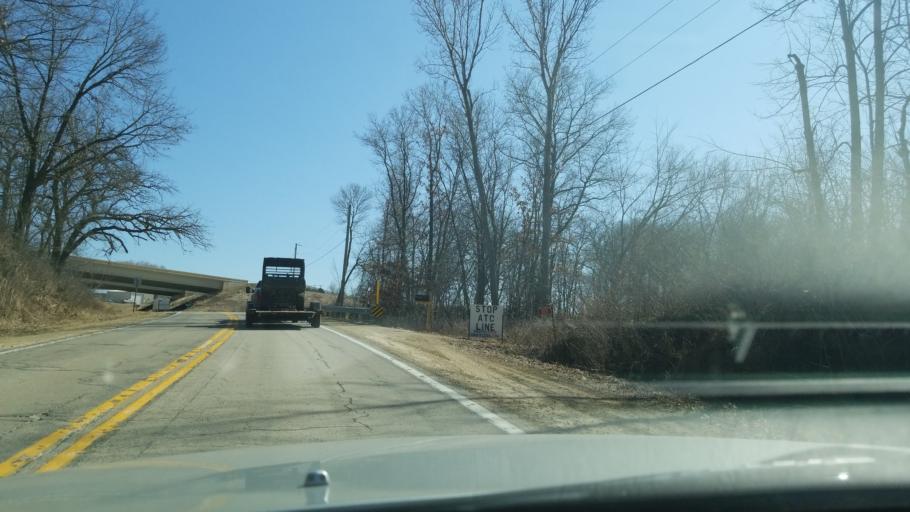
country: US
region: Wisconsin
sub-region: Iowa County
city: Mineral Point
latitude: 42.8628
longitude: -90.2043
